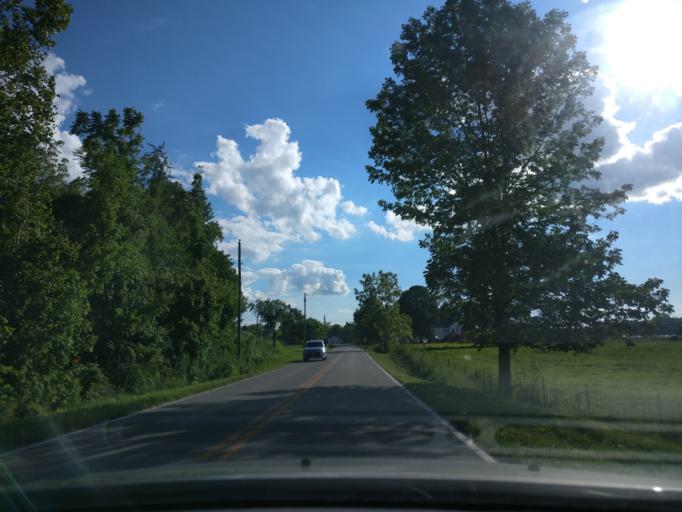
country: US
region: Ohio
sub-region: Clinton County
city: Wilmington
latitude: 39.4668
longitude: -83.8017
